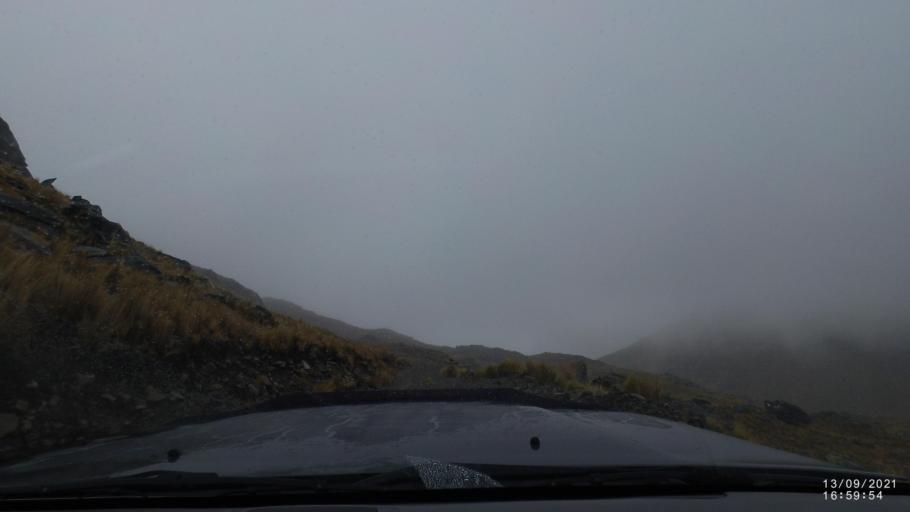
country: BO
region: Cochabamba
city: Colomi
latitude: -17.3117
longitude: -65.7167
